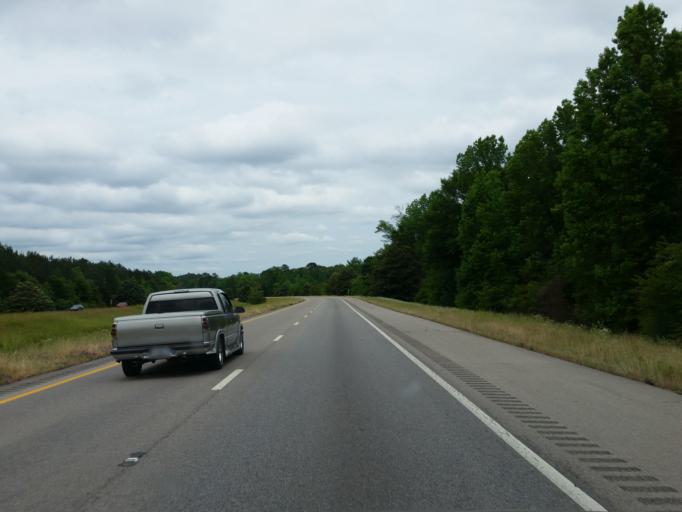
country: US
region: Mississippi
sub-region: Lauderdale County
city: Marion
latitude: 32.4110
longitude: -88.4806
